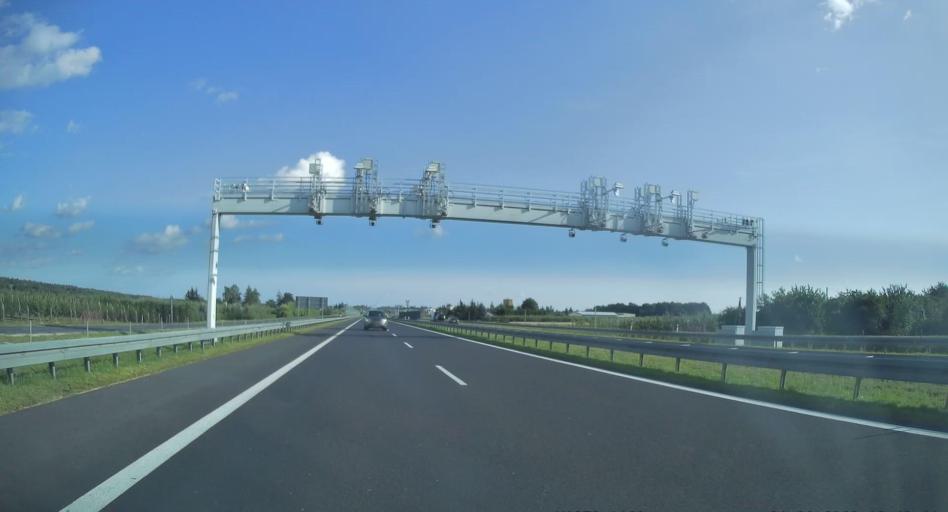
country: PL
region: Masovian Voivodeship
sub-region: Powiat bialobrzeski
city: Promna
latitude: 51.7061
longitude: 20.9275
